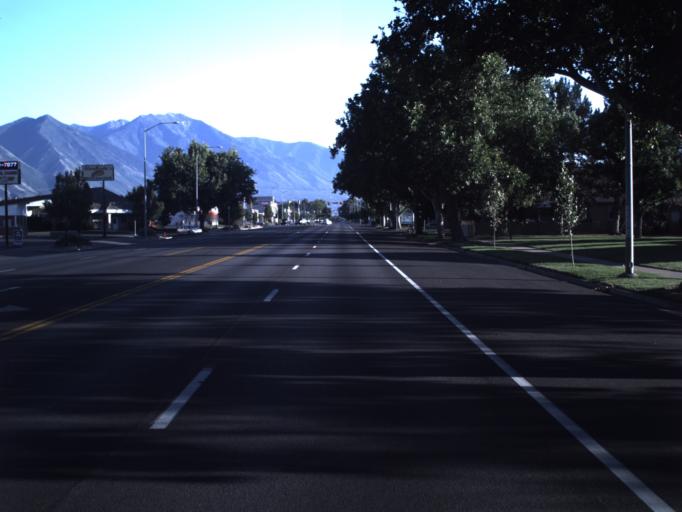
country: US
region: Utah
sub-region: Utah County
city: Spanish Fork
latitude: 40.1175
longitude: -111.6548
